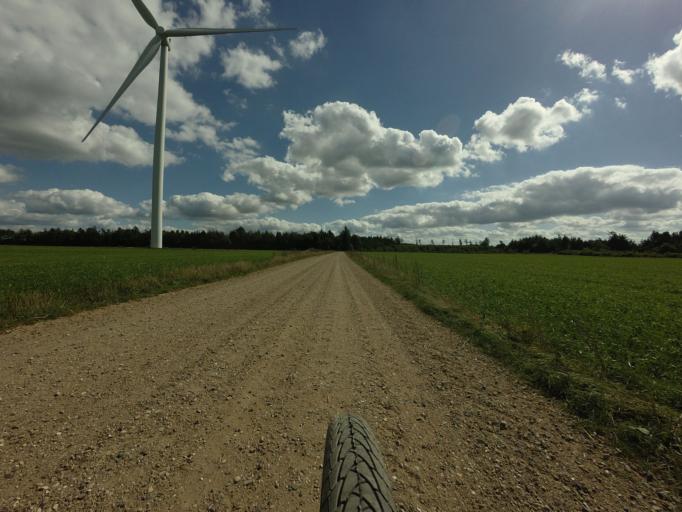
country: DK
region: Central Jutland
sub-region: Ikast-Brande Kommune
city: Brande
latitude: 55.9725
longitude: 9.1259
